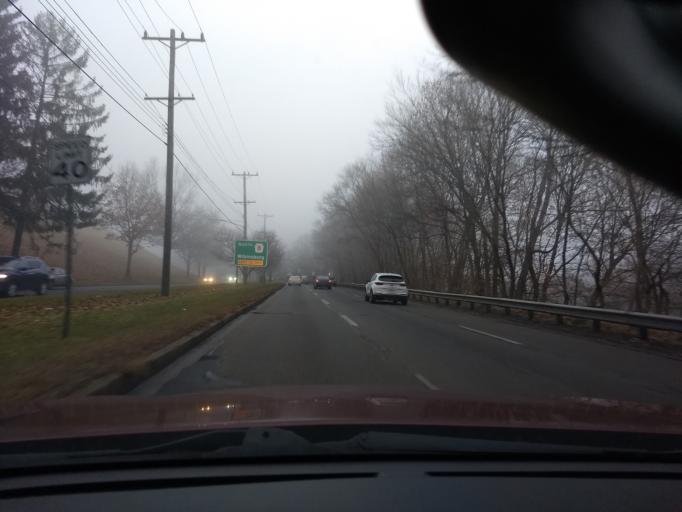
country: US
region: Pennsylvania
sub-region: Allegheny County
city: Braddock Hills
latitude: 40.4297
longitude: -79.8636
